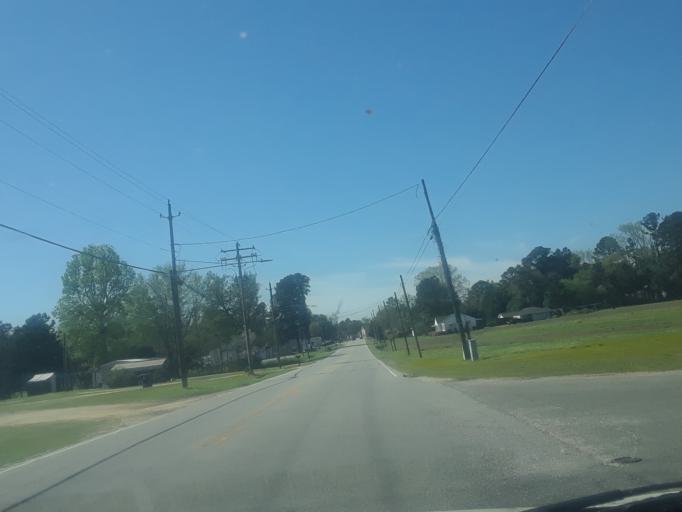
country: US
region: North Carolina
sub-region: Harnett County
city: Erwin
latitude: 35.3195
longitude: -78.6547
